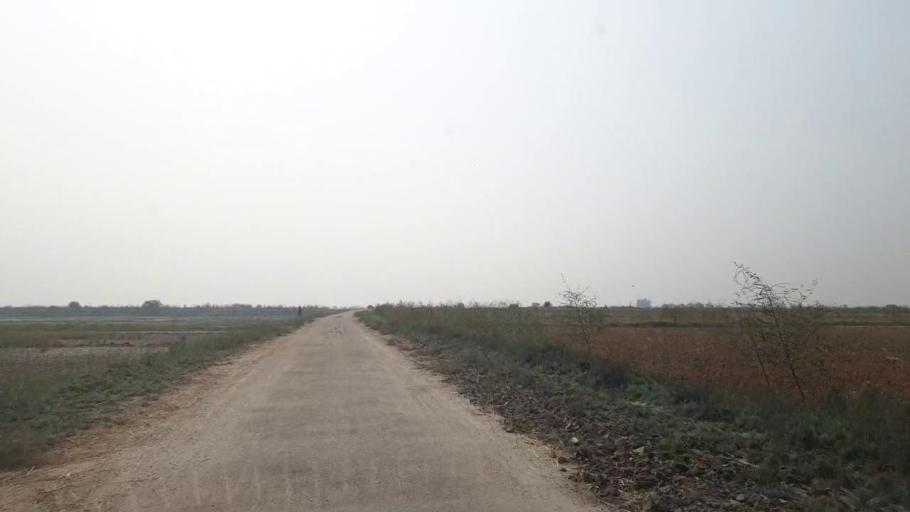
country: PK
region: Sindh
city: Matli
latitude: 25.1184
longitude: 68.6447
